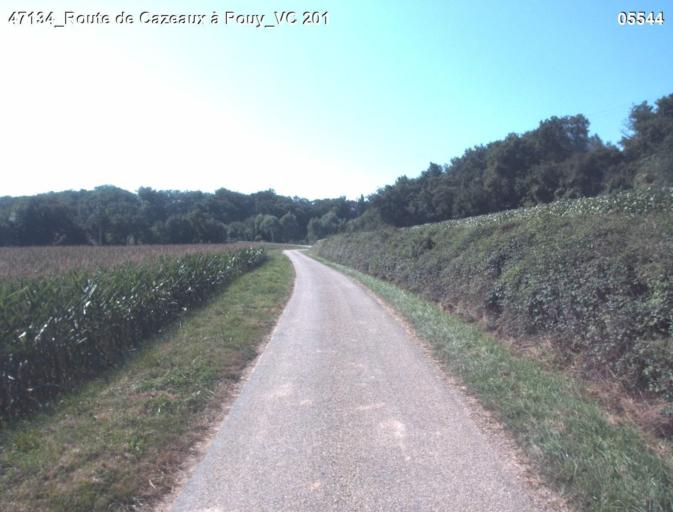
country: FR
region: Aquitaine
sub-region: Departement du Lot-et-Garonne
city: Mezin
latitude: 44.0446
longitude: 0.3092
